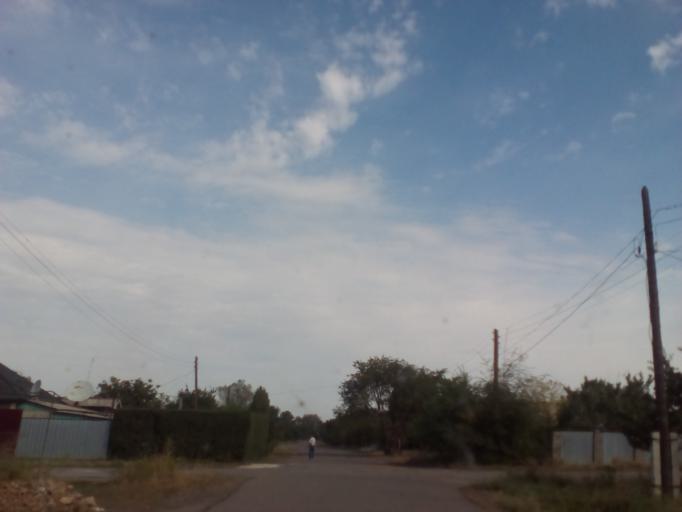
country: KZ
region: Almaty Oblysy
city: Burunday
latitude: 43.1665
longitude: 76.4051
